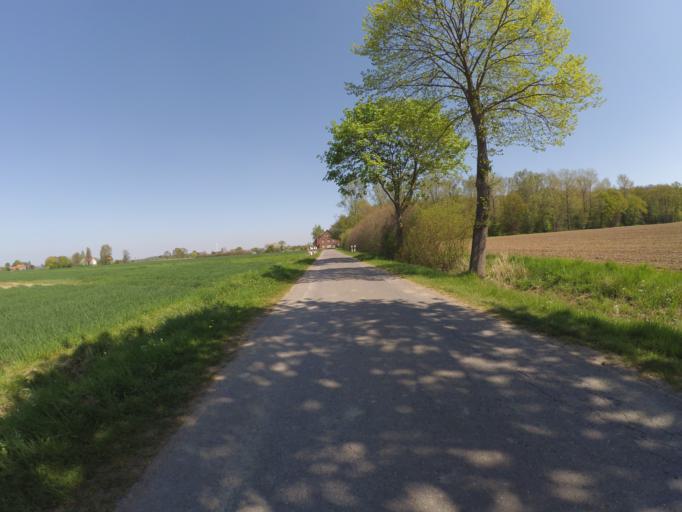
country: DE
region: North Rhine-Westphalia
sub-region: Regierungsbezirk Munster
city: Nordkirchen
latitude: 51.7718
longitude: 7.5564
